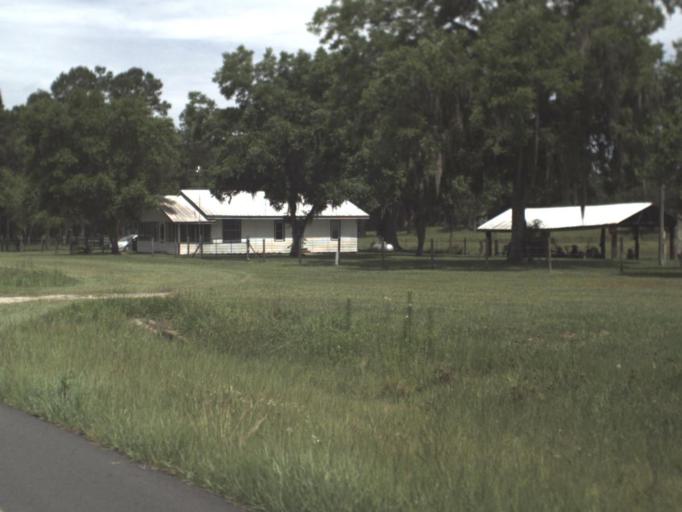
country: US
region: Florida
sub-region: Jefferson County
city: Monticello
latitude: 30.4922
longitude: -83.7271
